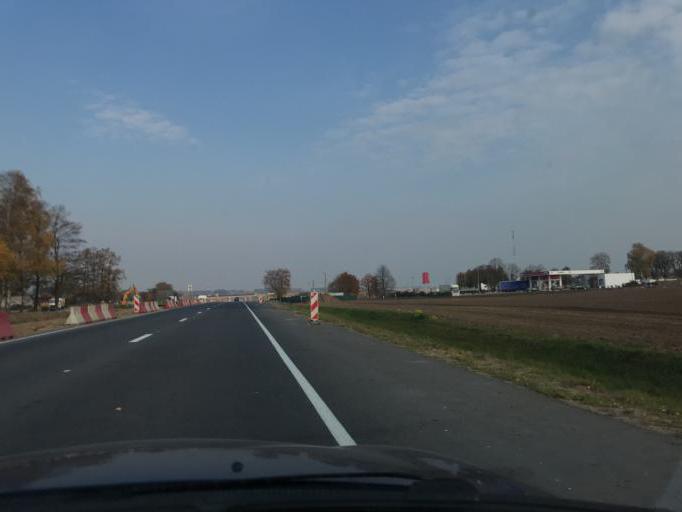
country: BY
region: Grodnenskaya
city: Shchuchin
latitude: 53.7264
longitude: 24.9739
